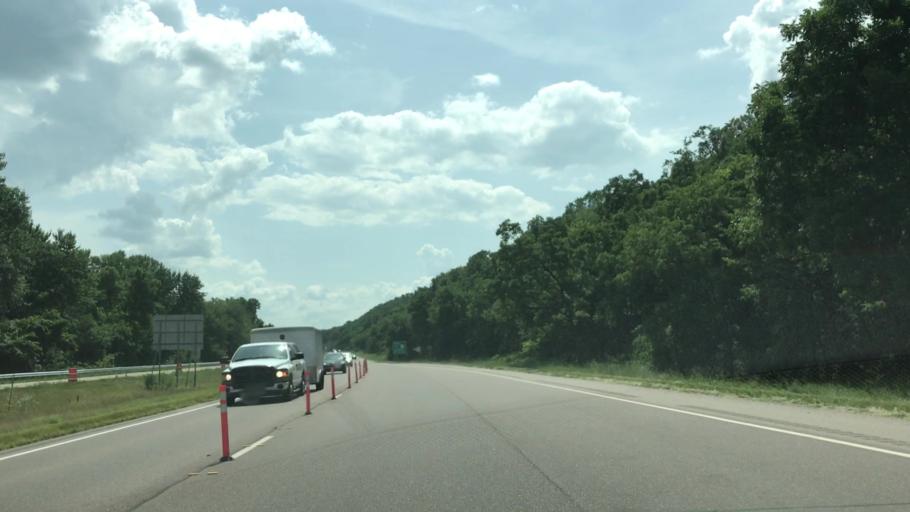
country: US
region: Minnesota
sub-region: Le Sueur County
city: Le Sueur
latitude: 44.4750
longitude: -93.9238
